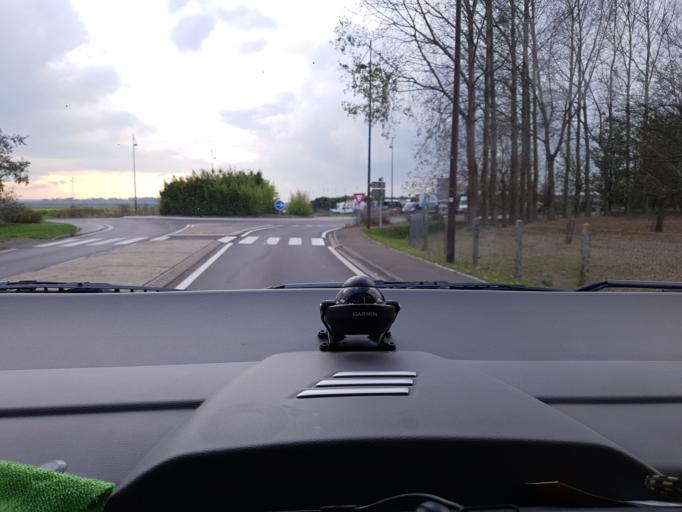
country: FR
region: Haute-Normandie
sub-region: Departement de la Seine-Maritime
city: Hautot-sur-Mer
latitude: 49.8912
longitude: 1.0323
